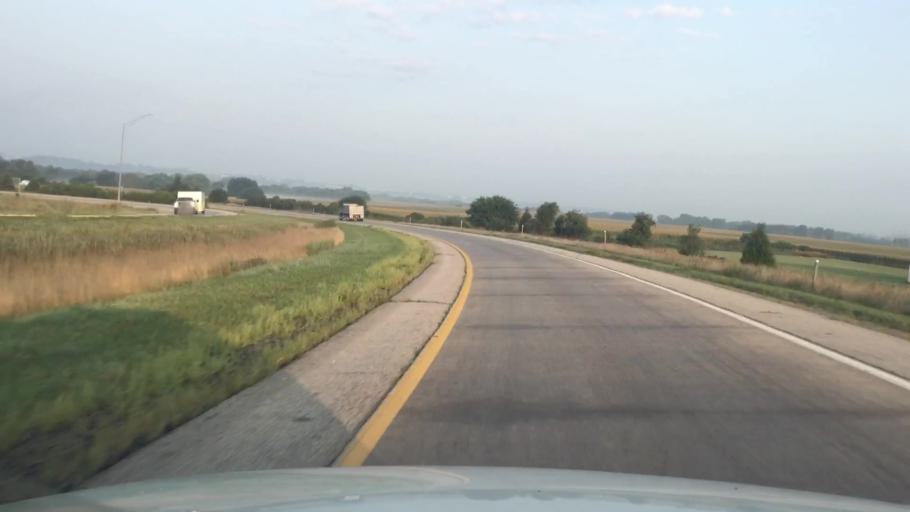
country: US
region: Iowa
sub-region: Polk County
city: Altoona
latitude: 41.6612
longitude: -93.5239
